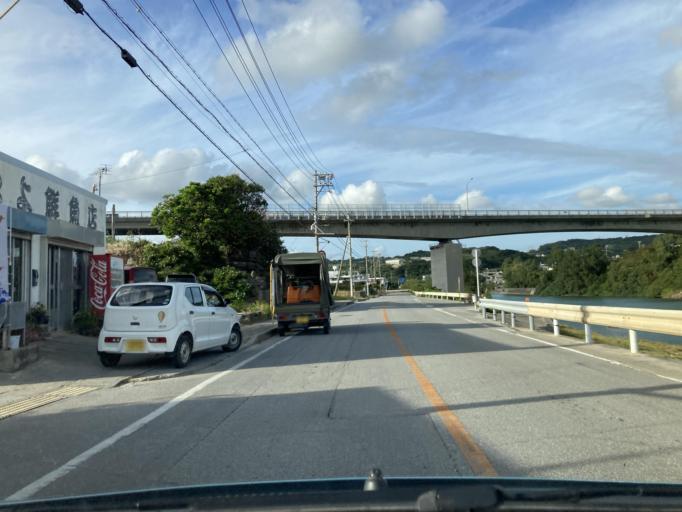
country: JP
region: Okinawa
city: Itoman
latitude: 26.1281
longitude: 127.7603
